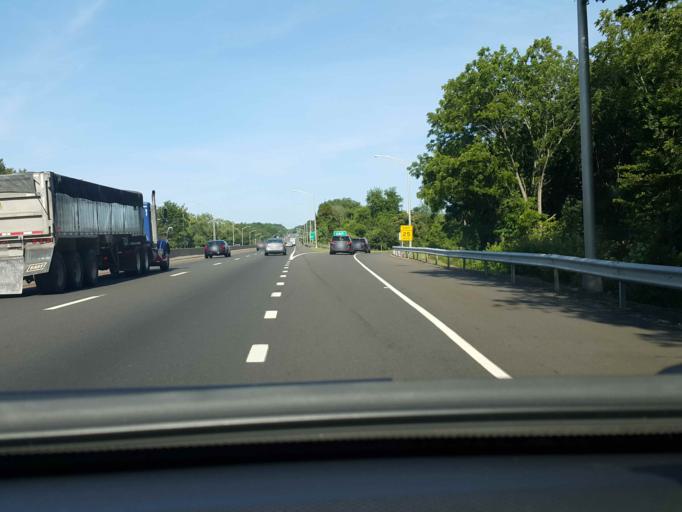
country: US
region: Connecticut
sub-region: New Haven County
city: Guilford
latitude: 41.2952
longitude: -72.6830
